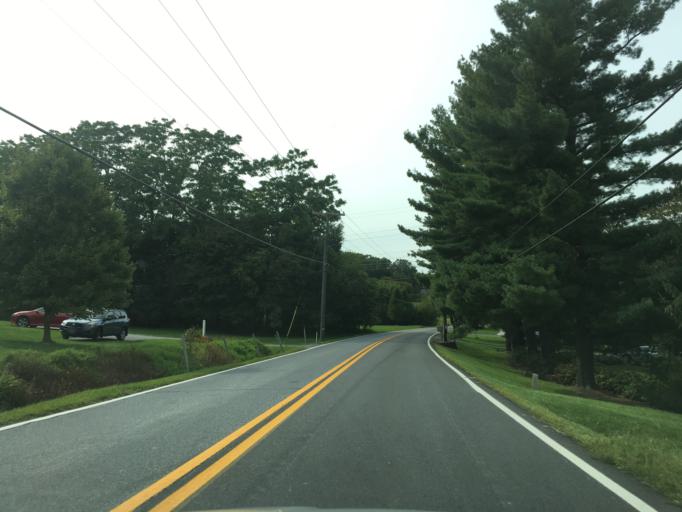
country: US
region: Maryland
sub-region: Baltimore County
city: Hunt Valley
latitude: 39.5849
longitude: -76.7225
